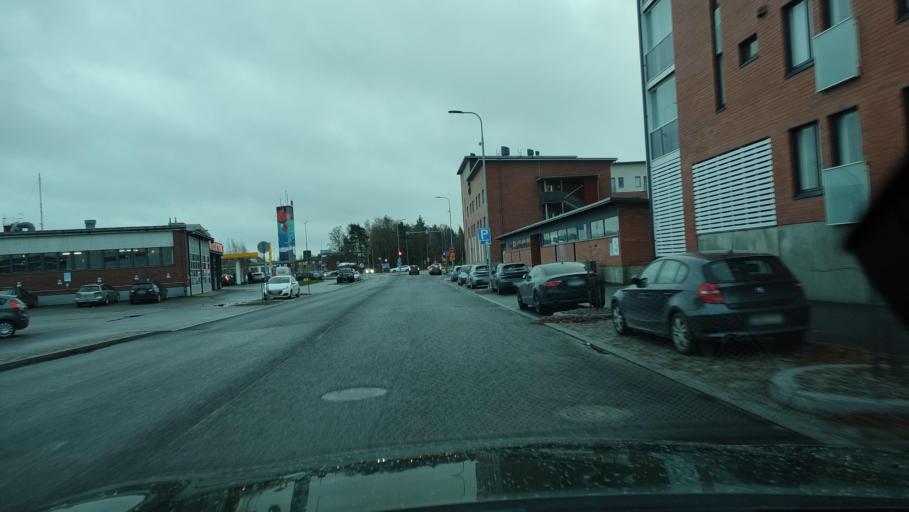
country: FI
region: Ostrobothnia
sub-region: Vaasa
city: Vaasa
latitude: 63.1015
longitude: 21.6344
